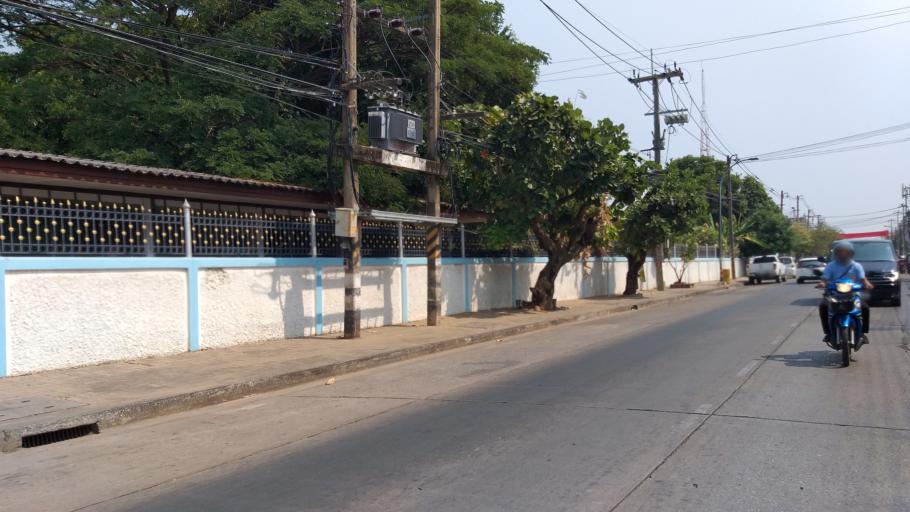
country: TH
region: Changwat Udon Thani
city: Udon Thani
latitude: 17.4068
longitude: 102.7778
